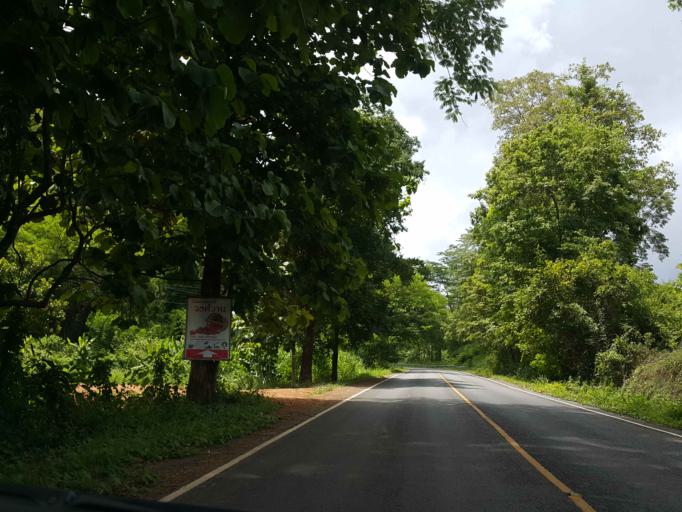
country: TH
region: Chiang Mai
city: Samoeng
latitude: 18.8088
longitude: 98.7896
